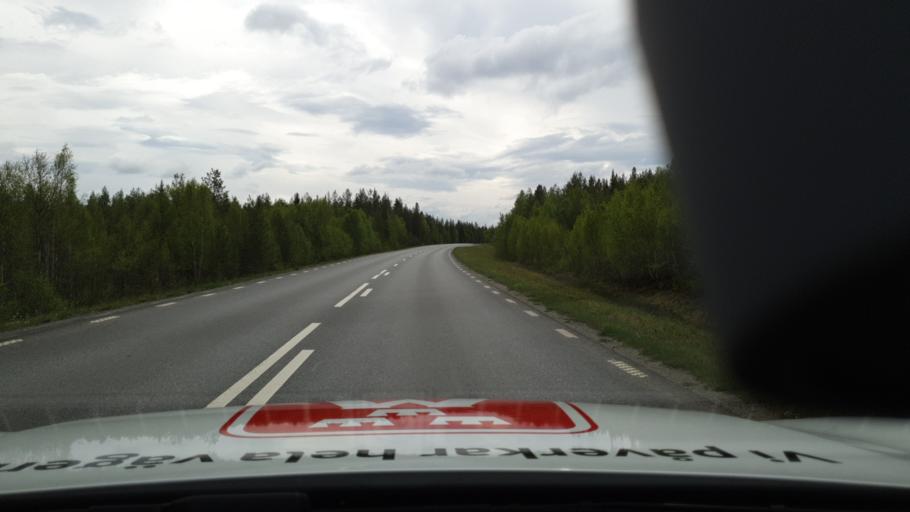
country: SE
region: Vaesterbotten
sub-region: Vilhelmina Kommun
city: Vilhelmina
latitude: 64.4286
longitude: 16.7794
